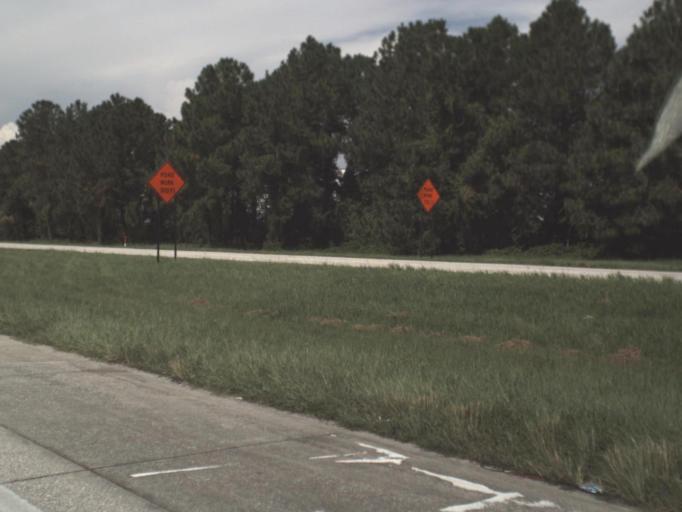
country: US
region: Florida
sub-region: Hillsborough County
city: Progress Village
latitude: 27.9171
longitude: -82.3366
